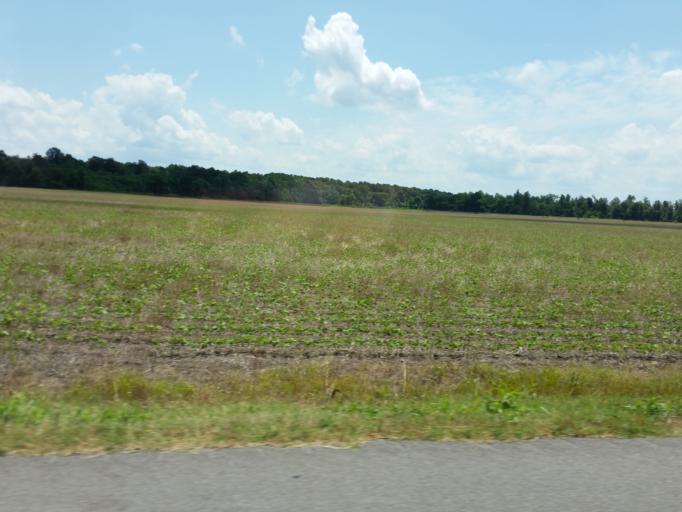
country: US
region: Tennessee
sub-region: Lake County
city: Tiptonville
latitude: 36.5072
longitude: -89.3522
